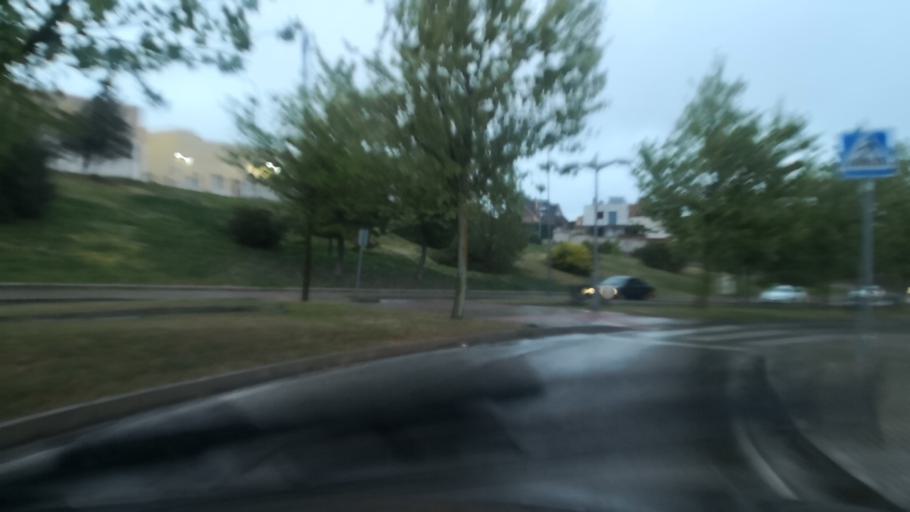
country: ES
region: Extremadura
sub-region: Provincia de Badajoz
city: Merida
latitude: 38.9051
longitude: -6.3639
